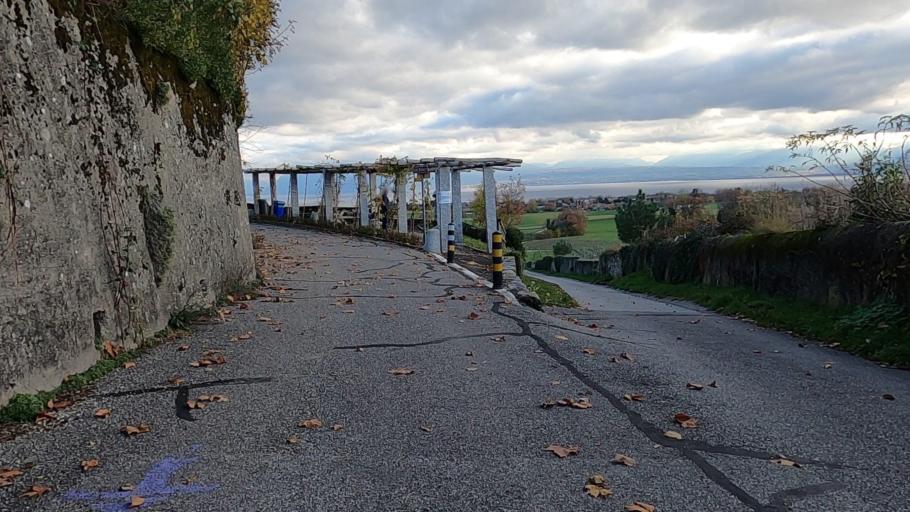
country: CH
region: Vaud
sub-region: Morges District
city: Saint-Prex
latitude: 46.5169
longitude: 6.4595
